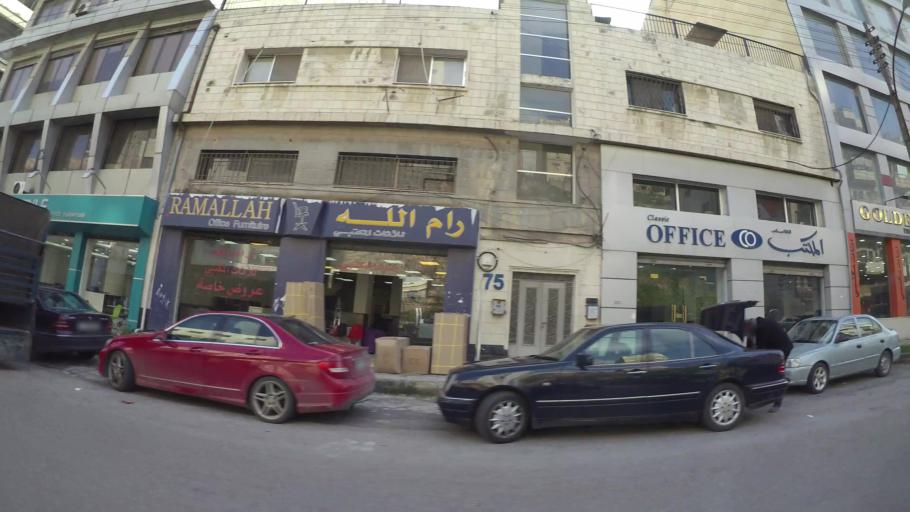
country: JO
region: Amman
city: Amman
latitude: 31.9560
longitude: 35.9151
